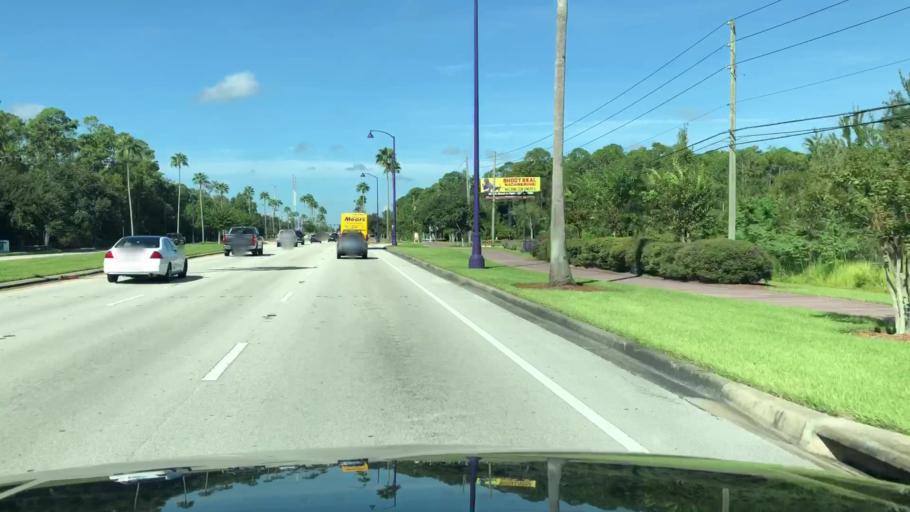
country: US
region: Florida
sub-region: Osceola County
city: Celebration
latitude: 28.3330
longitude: -81.5056
